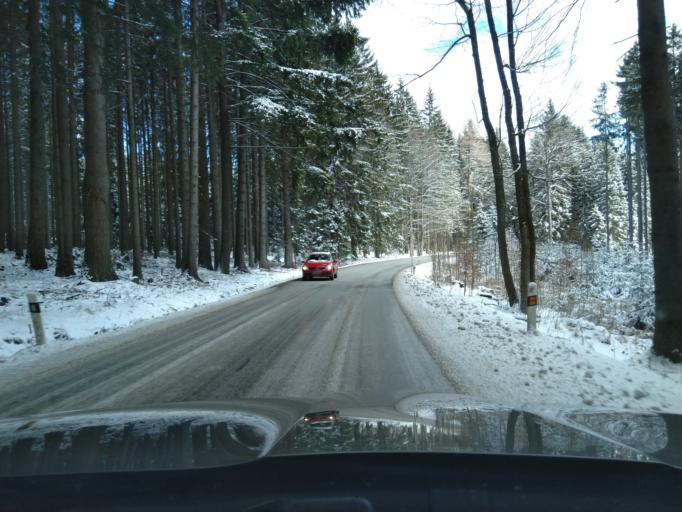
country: CZ
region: Jihocesky
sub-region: Okres Prachatice
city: Zdikov
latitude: 49.0510
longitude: 13.6895
